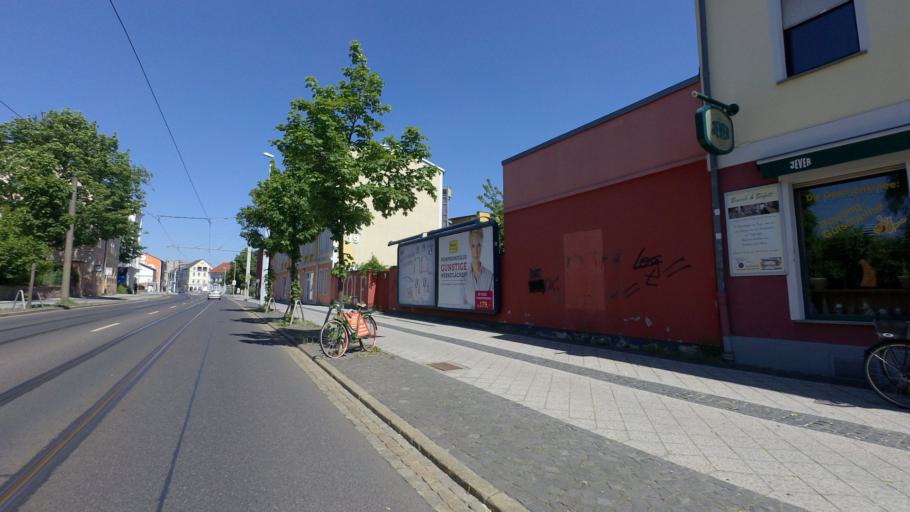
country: DE
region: Brandenburg
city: Cottbus
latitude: 51.7524
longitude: 14.3332
